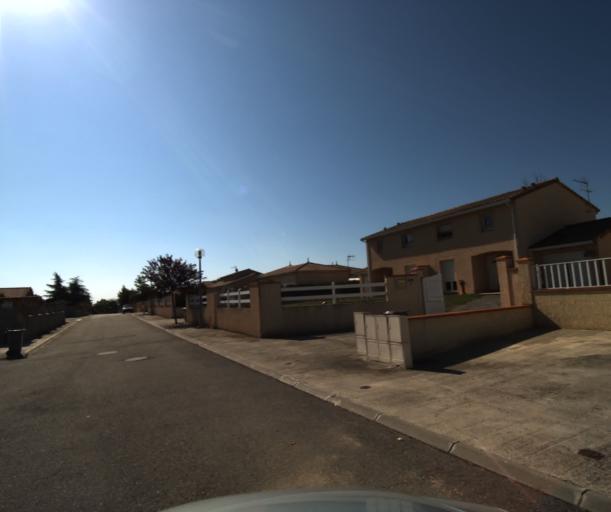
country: FR
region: Midi-Pyrenees
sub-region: Departement de la Haute-Garonne
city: Eaunes
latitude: 43.4300
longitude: 1.3542
